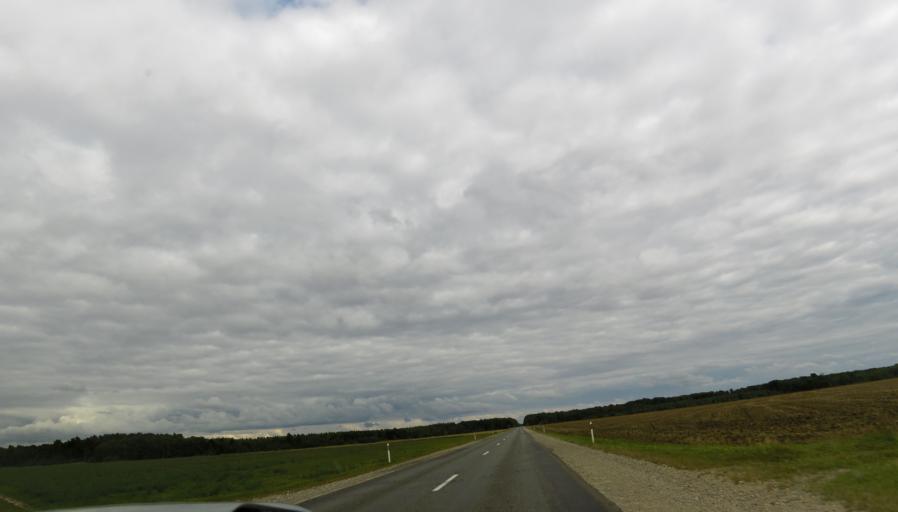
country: LT
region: Panevezys
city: Pasvalys
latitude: 56.0285
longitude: 24.2576
